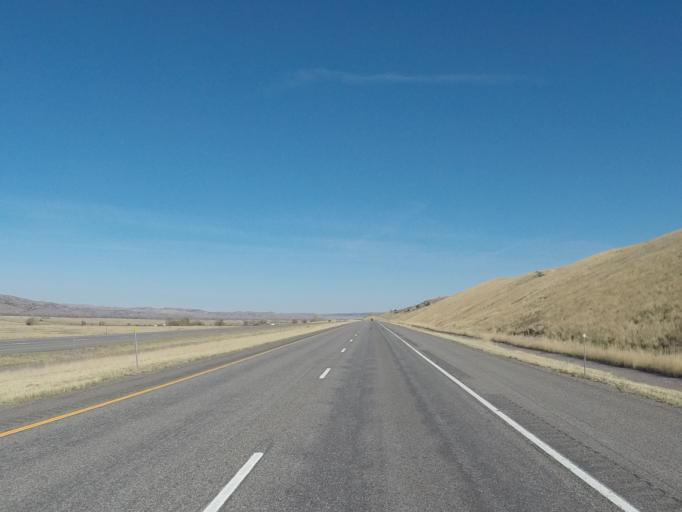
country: US
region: Montana
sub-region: Sweet Grass County
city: Big Timber
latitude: 45.7876
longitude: -110.0489
